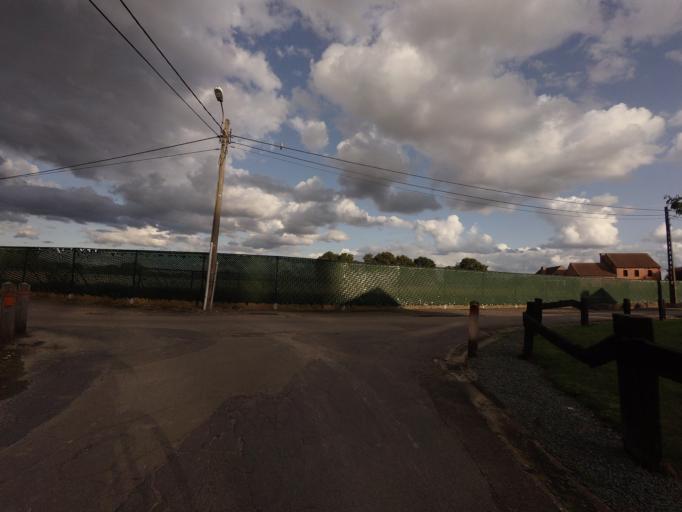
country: BE
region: Flanders
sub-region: Provincie Vlaams-Brabant
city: Londerzeel
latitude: 51.0013
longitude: 4.3187
